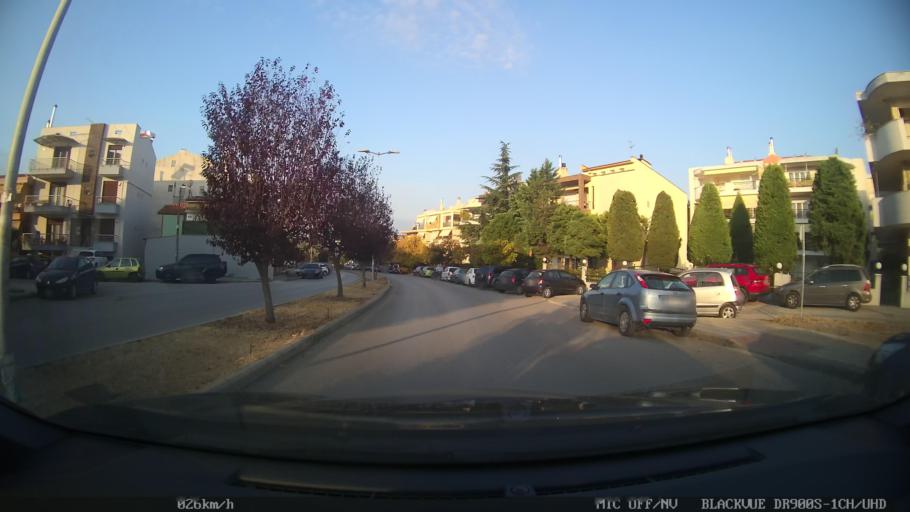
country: GR
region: Central Macedonia
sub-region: Nomos Thessalonikis
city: Pylaia
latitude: 40.5945
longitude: 22.9753
